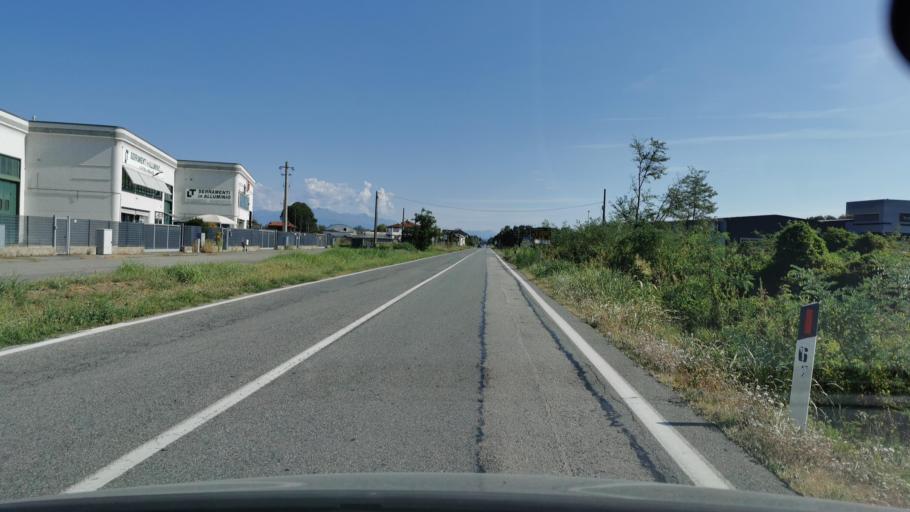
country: IT
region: Piedmont
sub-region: Provincia di Torino
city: Volpiano
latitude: 45.1788
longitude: 7.7668
